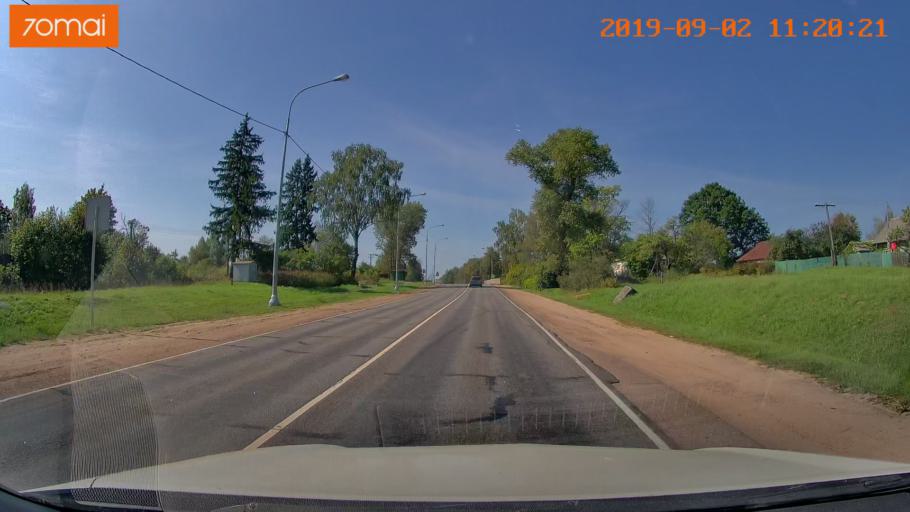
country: RU
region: Smolensk
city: Roslavl'
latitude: 54.0422
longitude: 33.0541
